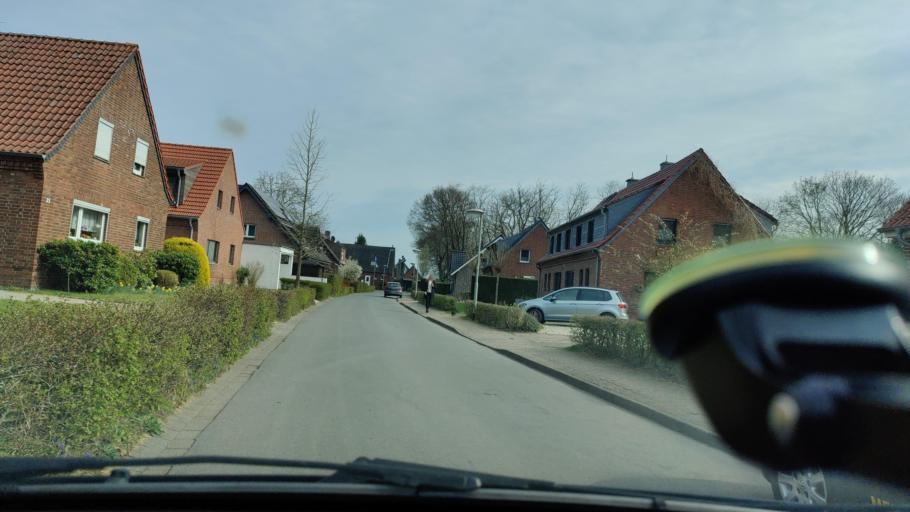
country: DE
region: North Rhine-Westphalia
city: Rheinberg
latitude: 51.5285
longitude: 6.6411
